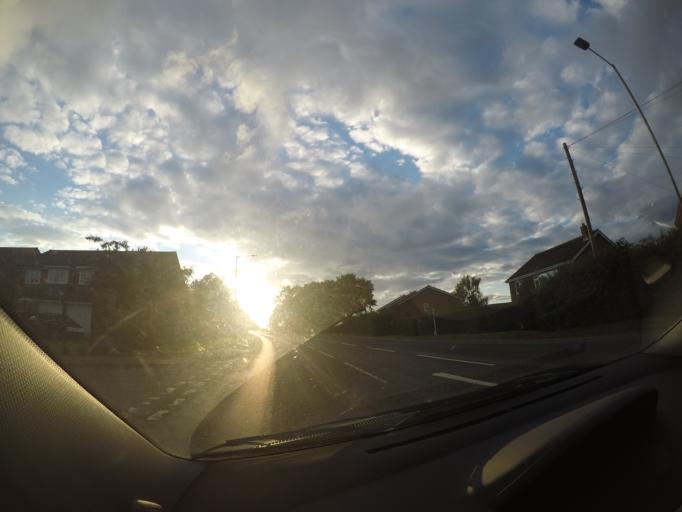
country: GB
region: England
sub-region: North Yorkshire
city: Catterick
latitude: 54.3792
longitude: -1.6346
